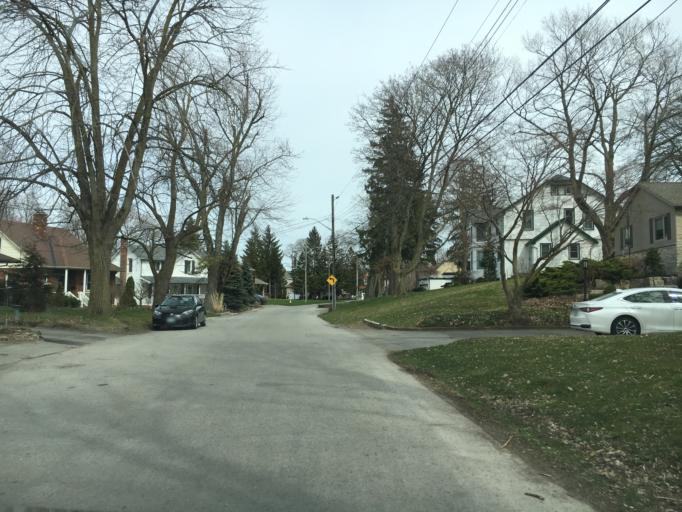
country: CA
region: Ontario
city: Port Colborne
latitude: 42.8795
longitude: -79.2625
